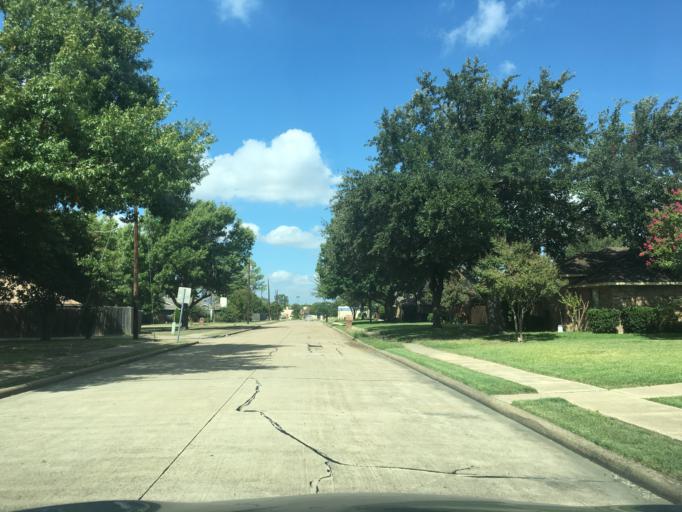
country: US
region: Texas
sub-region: Dallas County
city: Sachse
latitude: 32.9697
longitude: -96.5990
